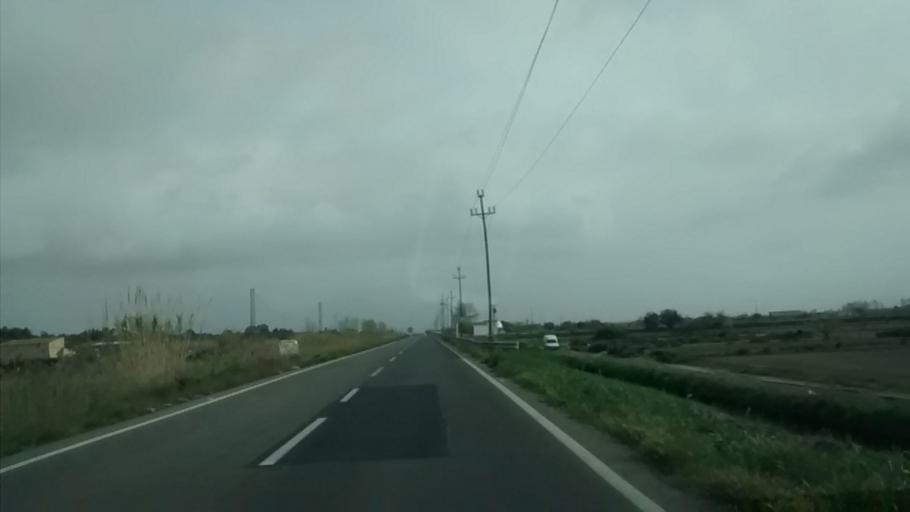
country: ES
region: Catalonia
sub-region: Provincia de Tarragona
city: Sant Carles de la Rapita
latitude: 40.6242
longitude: 0.5996
